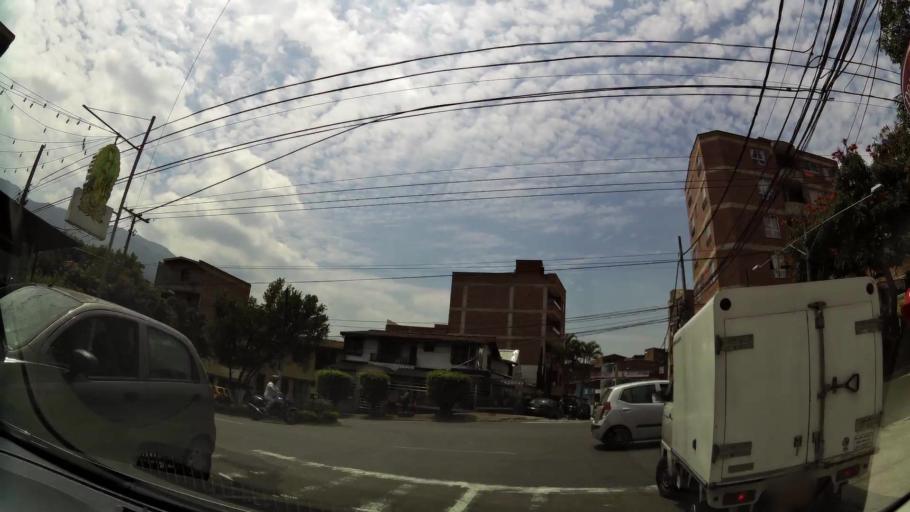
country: CO
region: Antioquia
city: Bello
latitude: 6.3142
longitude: -75.5609
